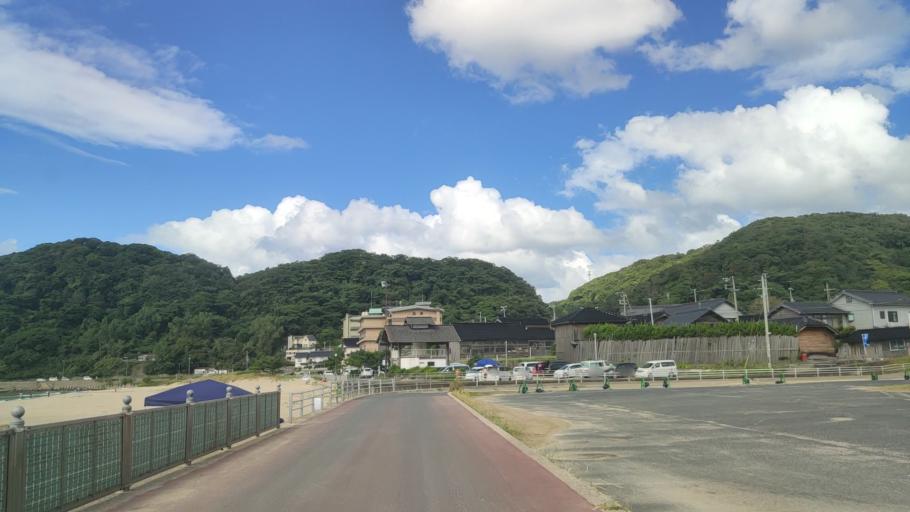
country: JP
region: Hyogo
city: Toyooka
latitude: 35.6660
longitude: 134.9671
